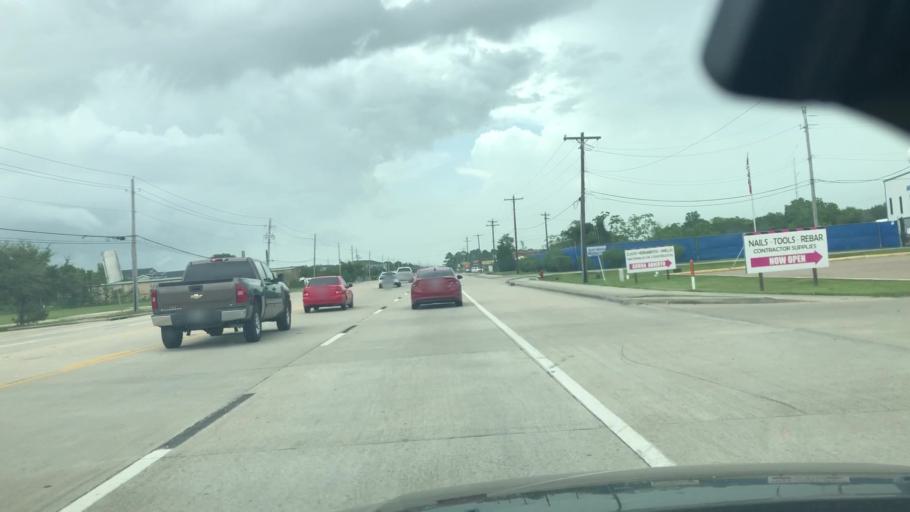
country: US
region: Texas
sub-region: Galveston County
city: Dickinson
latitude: 29.4715
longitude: -95.0824
